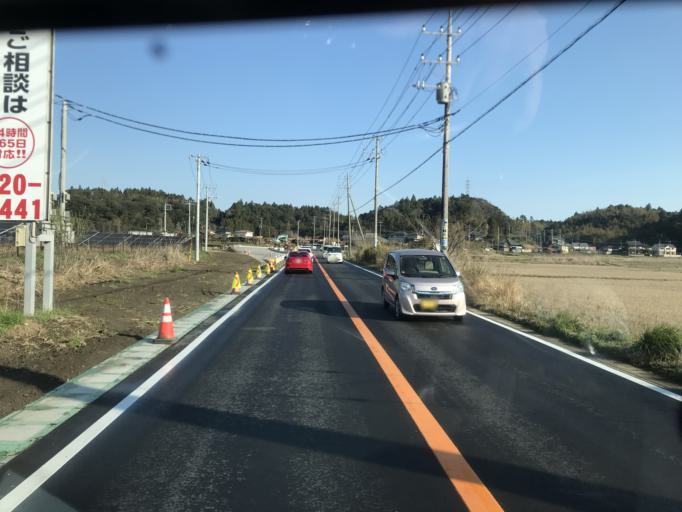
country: JP
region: Chiba
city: Sawara
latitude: 35.8740
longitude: 140.4955
